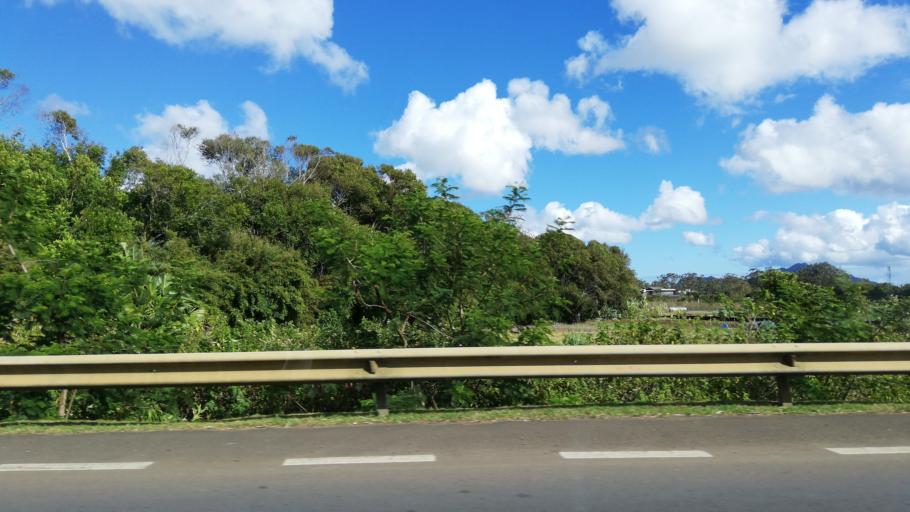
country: MU
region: Moka
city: La Dagotiere
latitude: -20.2551
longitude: 57.5635
